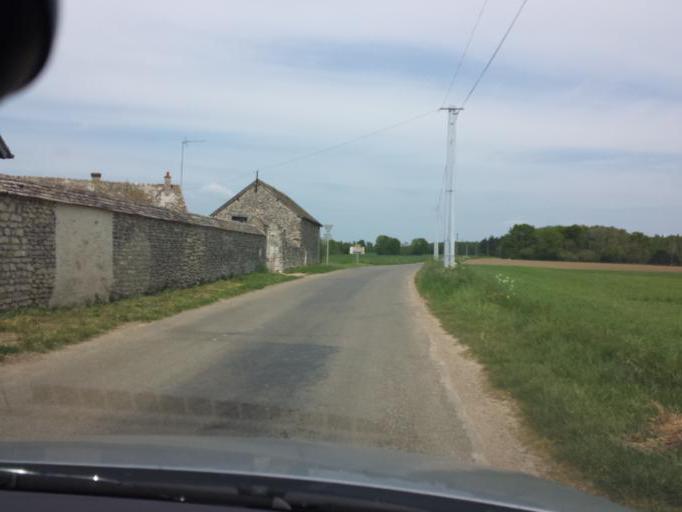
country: FR
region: Ile-de-France
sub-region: Departement des Yvelines
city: Houdan
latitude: 48.8508
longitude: 1.5567
